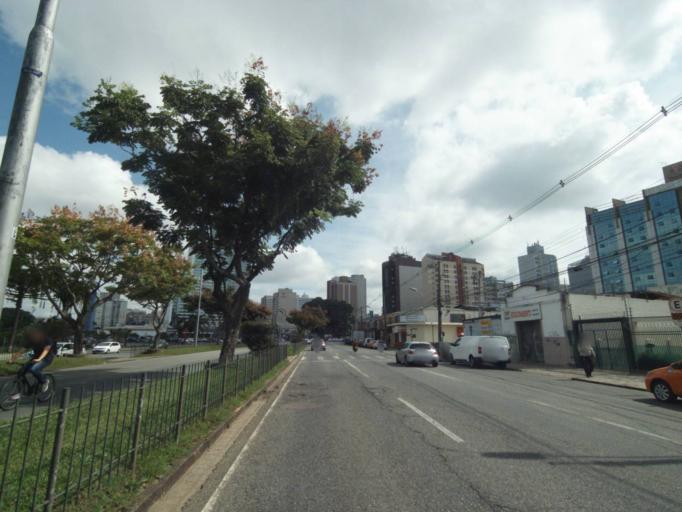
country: BR
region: Parana
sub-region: Curitiba
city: Curitiba
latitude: -25.4356
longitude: -49.2587
